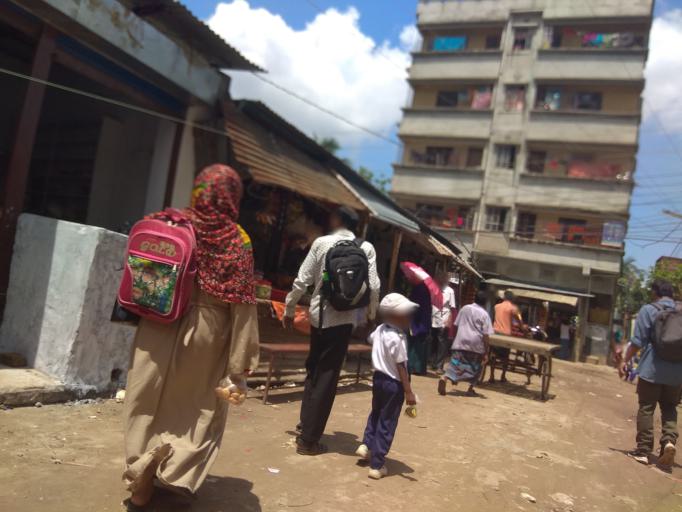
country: BD
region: Dhaka
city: Tungi
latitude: 23.8274
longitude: 90.3869
